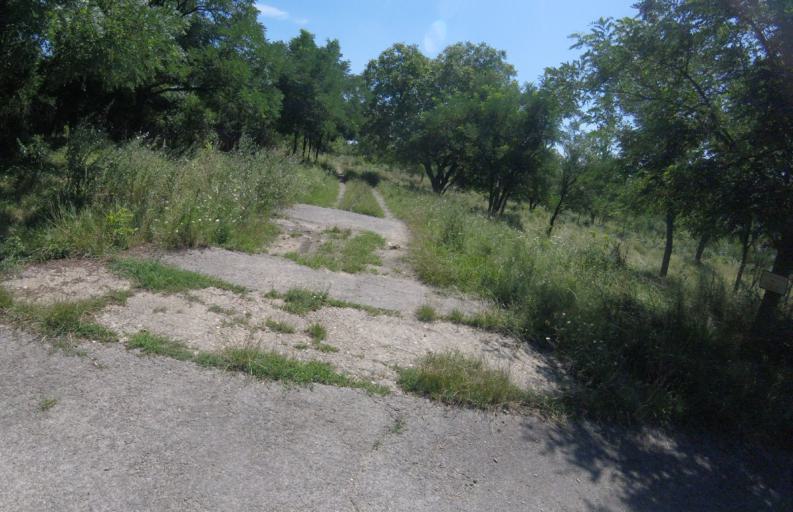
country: HU
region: Pest
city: Szob
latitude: 47.8705
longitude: 18.8712
